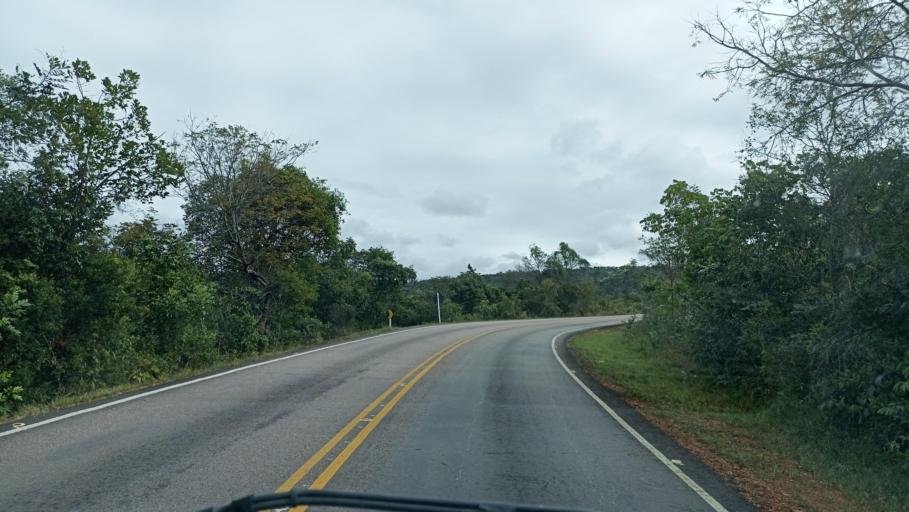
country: BR
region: Bahia
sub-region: Andarai
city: Vera Cruz
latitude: -12.9326
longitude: -41.2400
